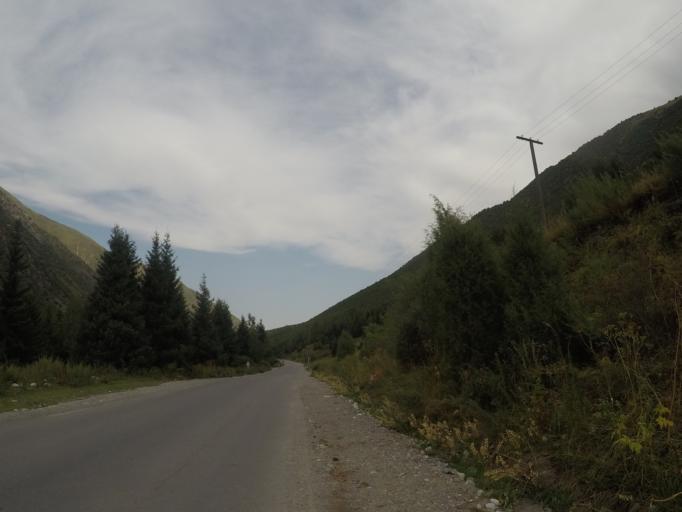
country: KG
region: Chuy
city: Bishkek
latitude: 42.5917
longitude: 74.4833
